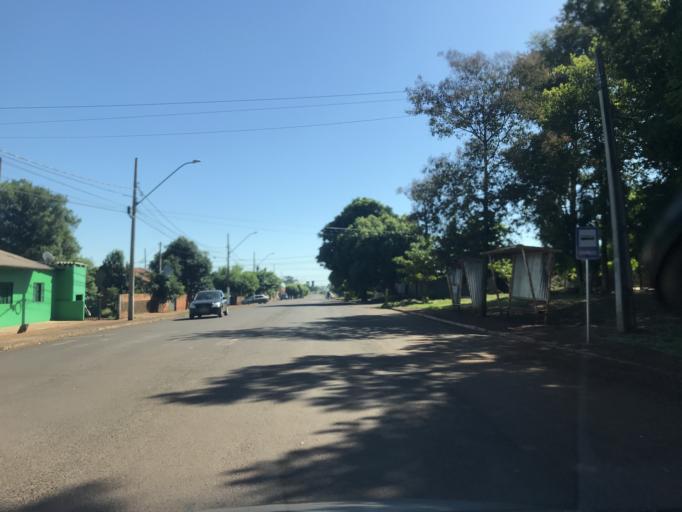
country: BR
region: Parana
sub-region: Palotina
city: Palotina
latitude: -24.2704
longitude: -53.8451
